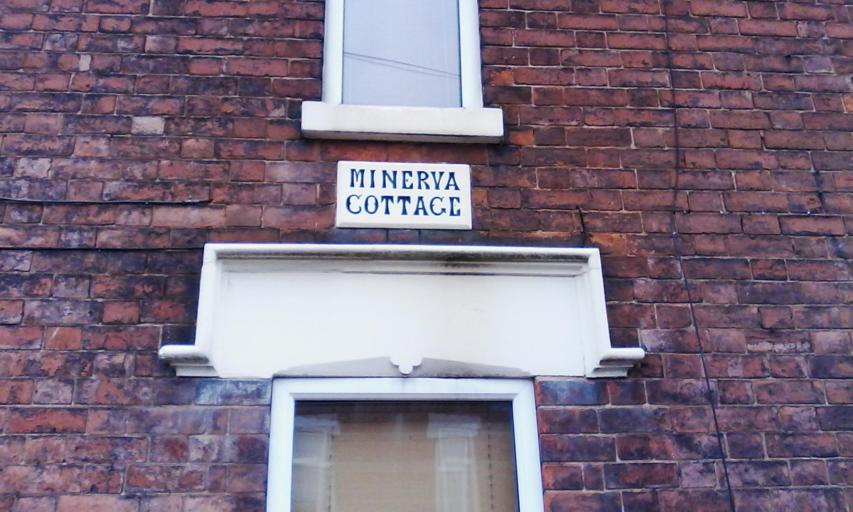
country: GB
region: England
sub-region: Nottinghamshire
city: Arnold
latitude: 52.9701
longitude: -1.0964
